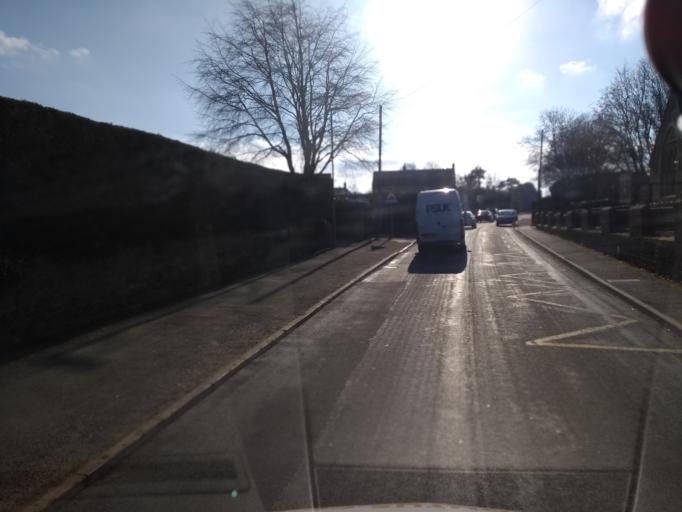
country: GB
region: England
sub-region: Somerset
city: South Petherton
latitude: 50.9453
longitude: -2.8034
